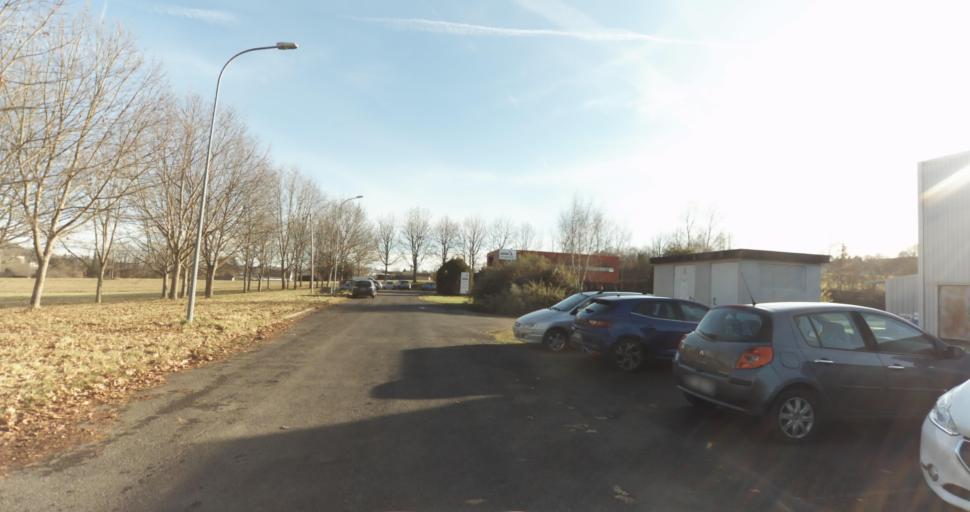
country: FR
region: Limousin
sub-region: Departement de la Haute-Vienne
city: Aixe-sur-Vienne
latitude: 45.8029
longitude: 1.1182
